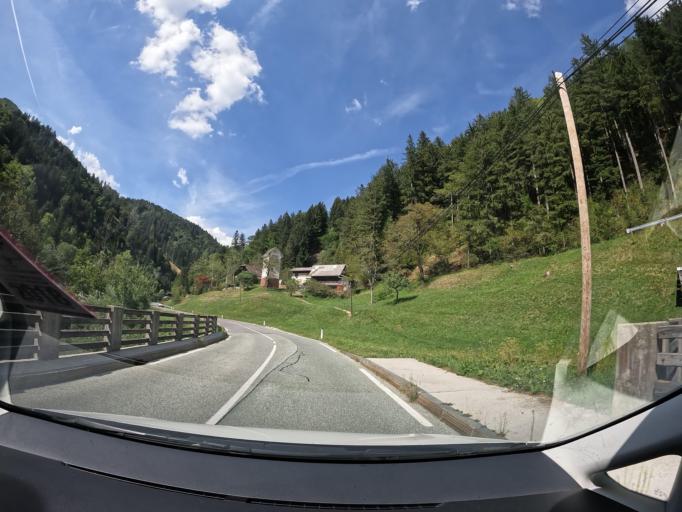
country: SI
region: Jezersko
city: Zgornje Jezersko
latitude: 46.3254
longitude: 14.4917
